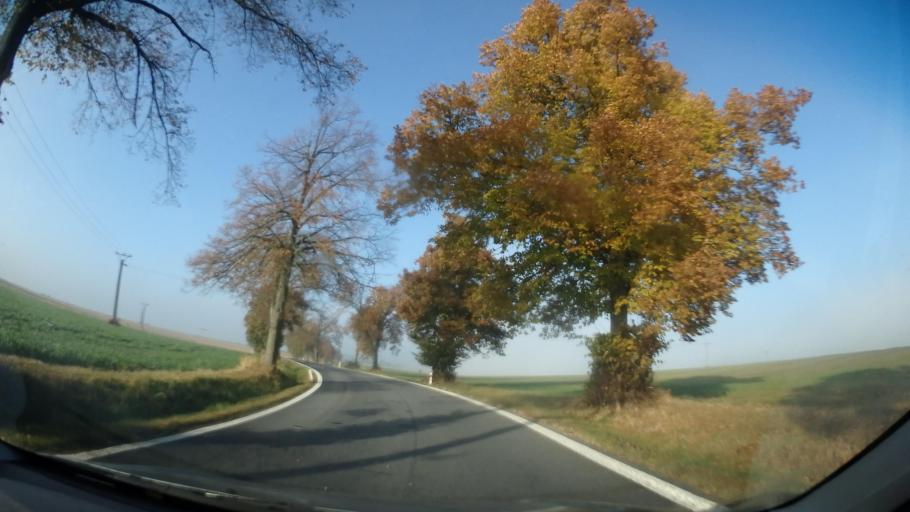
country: CZ
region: Vysocina
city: Krizanov
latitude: 49.4387
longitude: 16.1670
